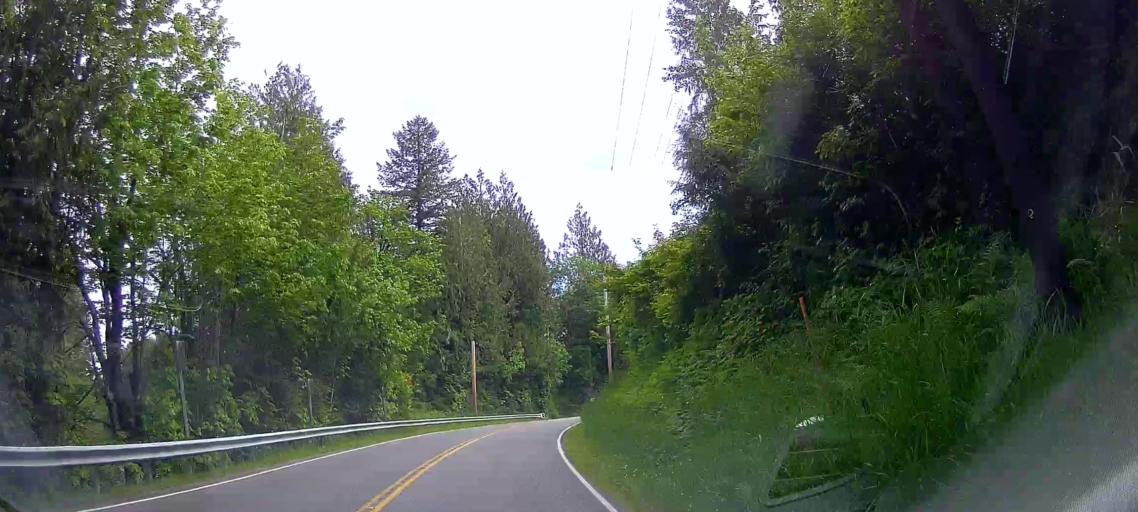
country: US
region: Washington
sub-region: Snohomish County
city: Bryant
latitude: 48.2389
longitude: -122.2009
